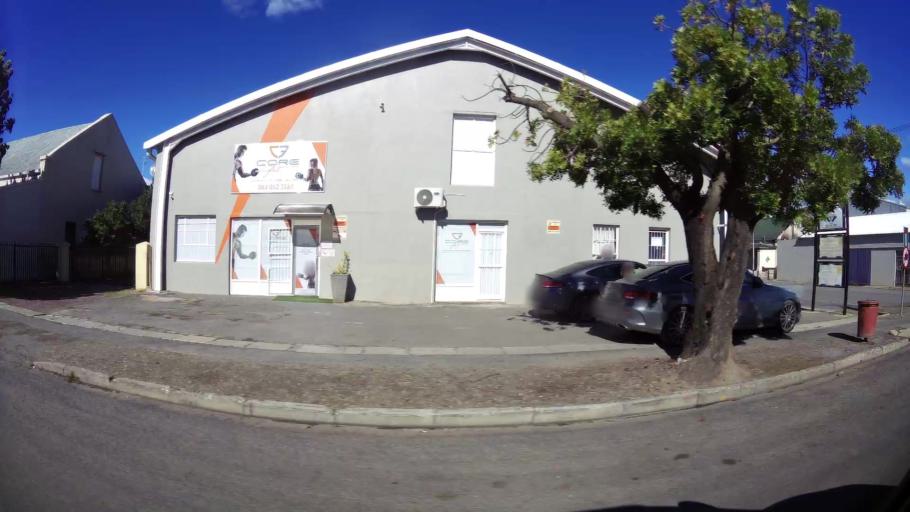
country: ZA
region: Western Cape
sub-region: Cape Winelands District Municipality
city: Ashton
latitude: -33.8076
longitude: 19.8810
